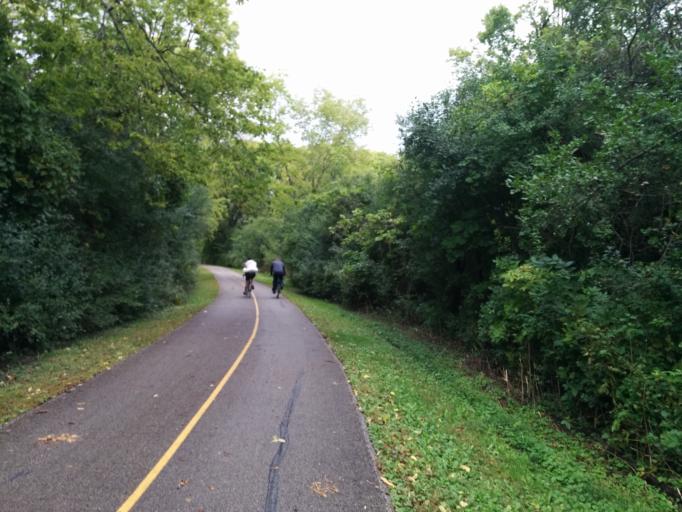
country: US
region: Illinois
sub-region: Cook County
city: Northfield
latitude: 42.1110
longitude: -87.7736
